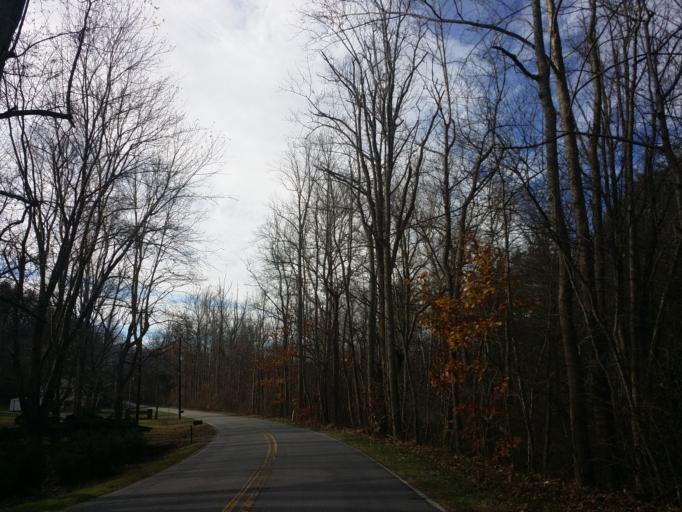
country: US
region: North Carolina
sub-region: Buncombe County
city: Swannanoa
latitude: 35.6259
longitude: -82.4296
